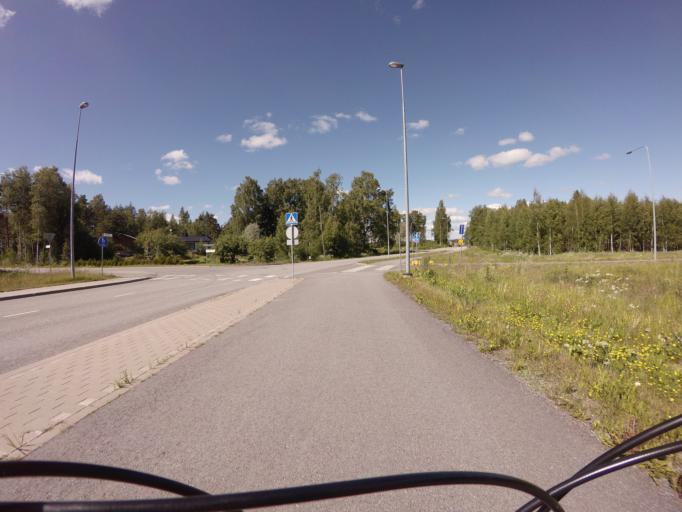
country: FI
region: Varsinais-Suomi
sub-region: Turku
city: Turku
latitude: 60.5106
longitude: 22.2898
